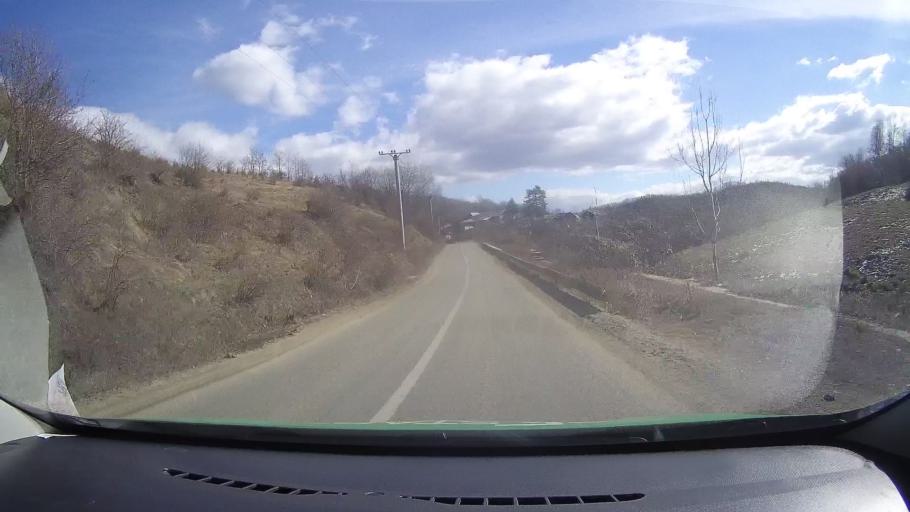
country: RO
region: Dambovita
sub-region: Comuna Glodeni
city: Laculete
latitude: 45.0241
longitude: 25.4305
